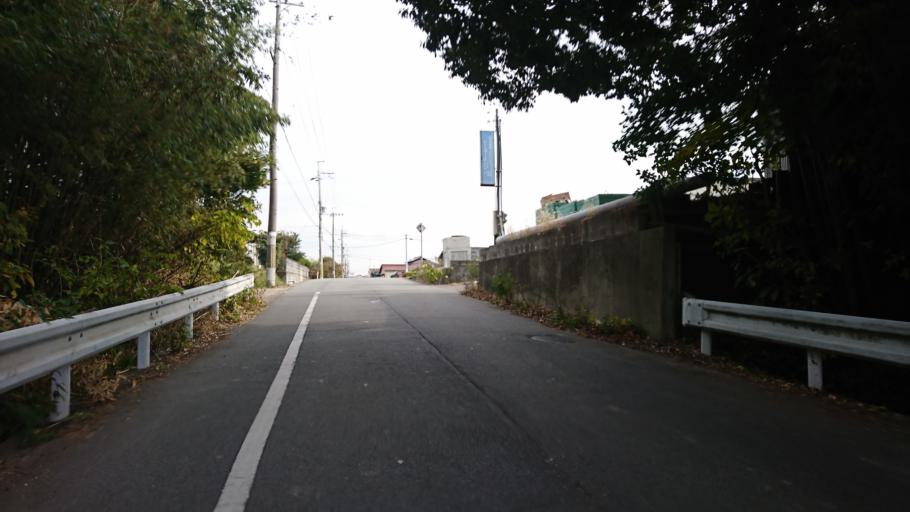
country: JP
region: Hyogo
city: Kakogawacho-honmachi
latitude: 34.7678
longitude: 134.8599
